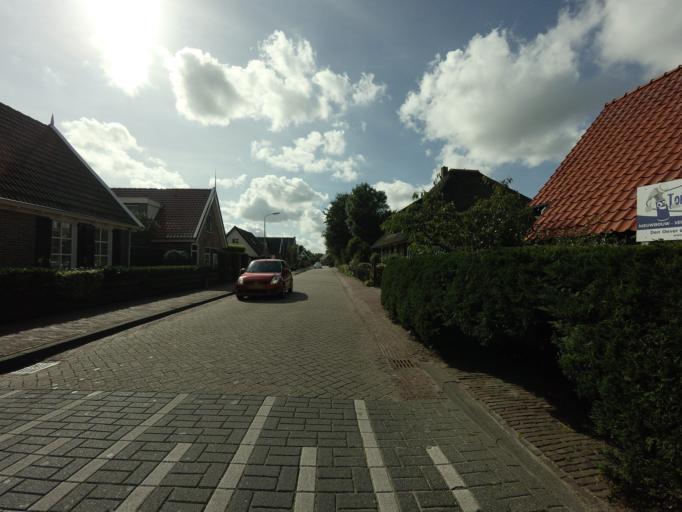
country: NL
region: North Holland
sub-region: Gemeente Hollands Kroon
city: Den Oever
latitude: 52.9046
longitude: 4.9514
